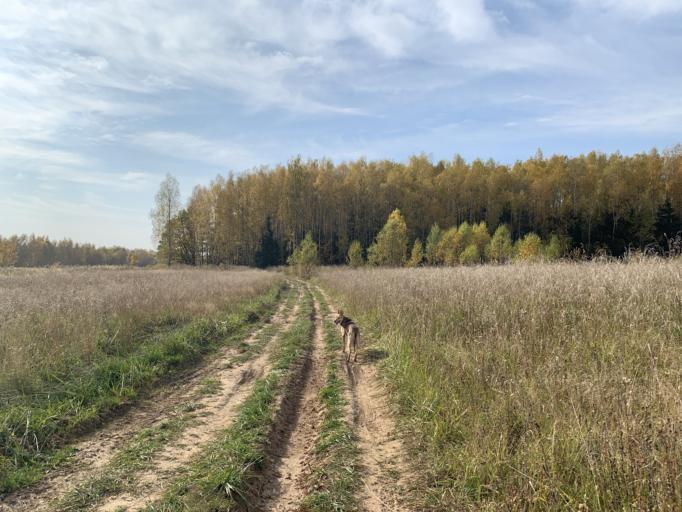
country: RU
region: Jaroslavl
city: Porech'ye-Rybnoye
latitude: 56.9895
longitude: 39.4010
